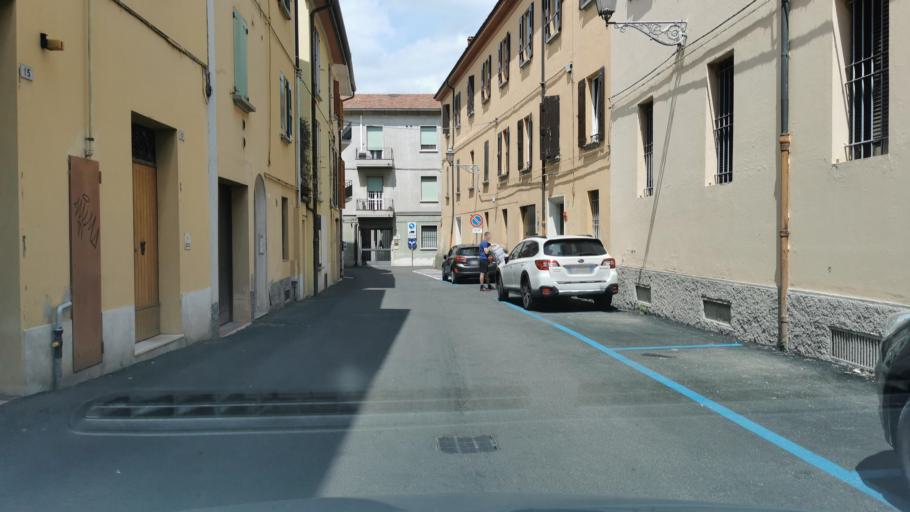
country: IT
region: Emilia-Romagna
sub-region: Provincia di Bologna
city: Castel San Pietro Terme
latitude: 44.3977
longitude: 11.5908
